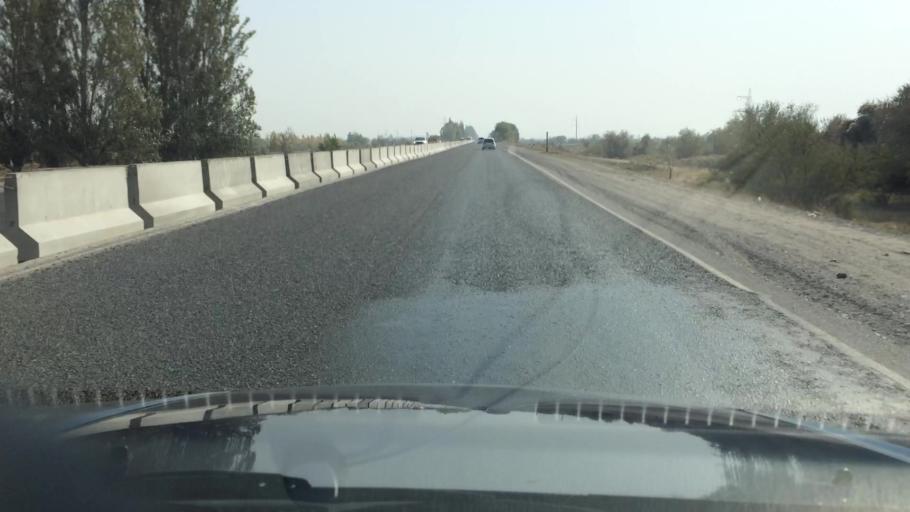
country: KG
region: Chuy
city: Kant
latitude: 42.9720
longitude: 74.8999
